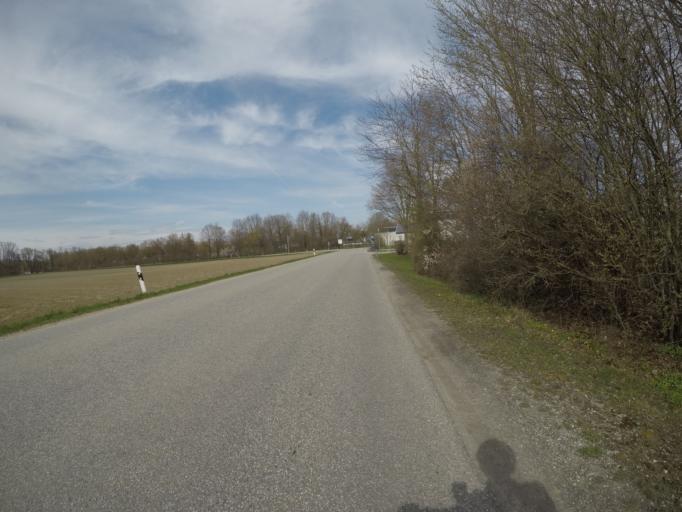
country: DE
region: Bavaria
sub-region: Lower Bavaria
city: Ergolding
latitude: 48.5555
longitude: 12.1954
